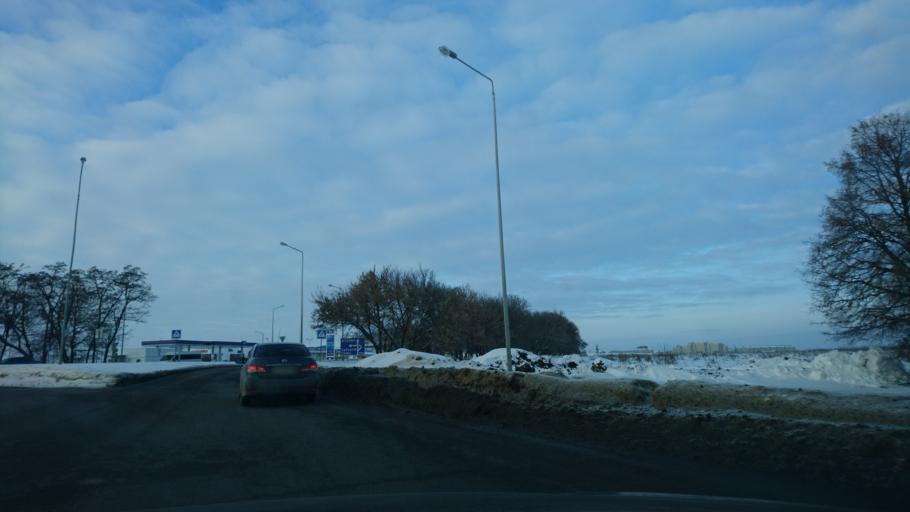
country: RU
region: Belgorod
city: Severnyy
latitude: 50.6611
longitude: 36.5637
